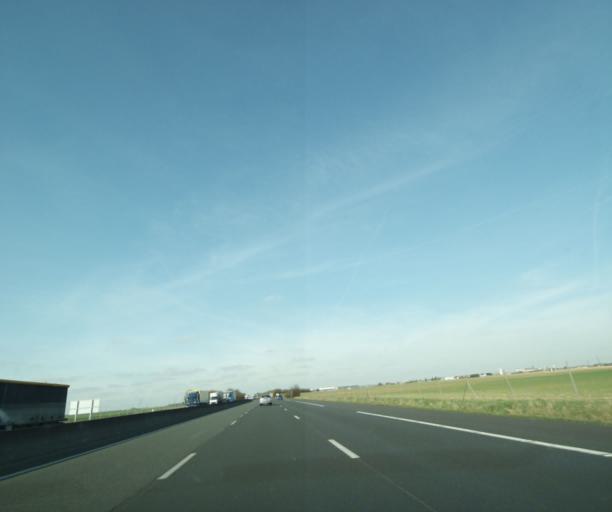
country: FR
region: Centre
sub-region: Departement du Loiret
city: Artenay
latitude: 48.0690
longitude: 1.8480
